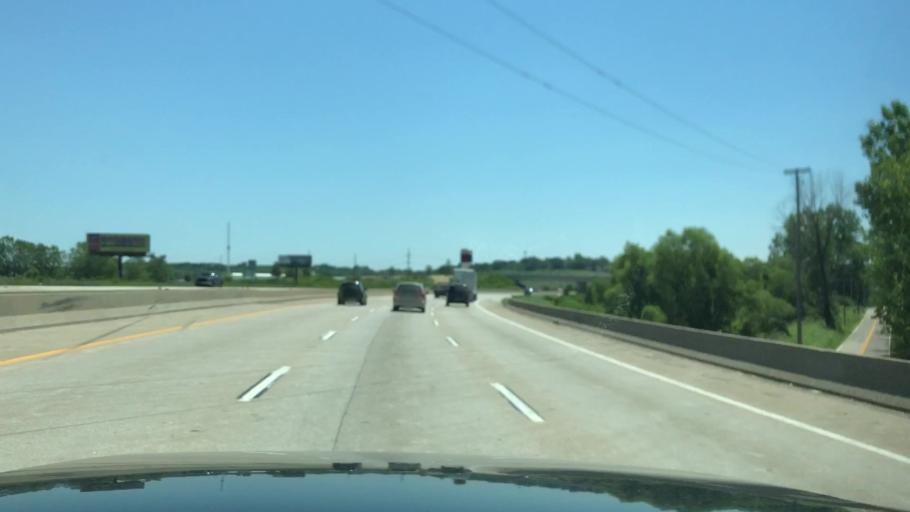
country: US
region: Missouri
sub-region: Saint Louis County
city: Bridgeton
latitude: 38.7893
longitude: -90.4245
